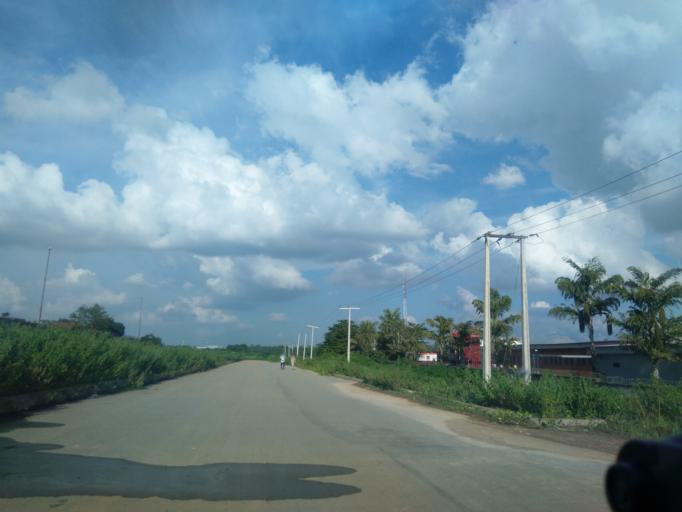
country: NG
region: Abuja Federal Capital Territory
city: Abuja
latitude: 9.0294
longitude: 7.4082
